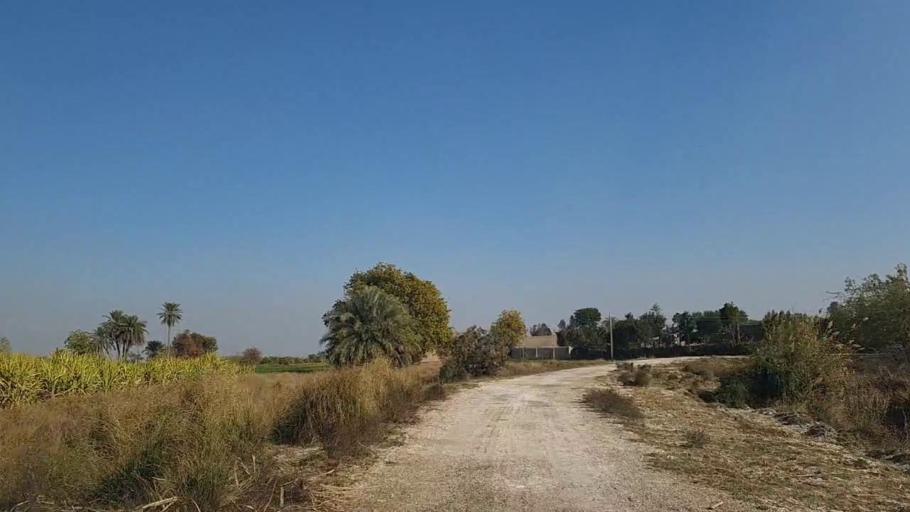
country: PK
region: Sindh
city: Bandhi
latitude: 26.5727
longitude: 68.3103
